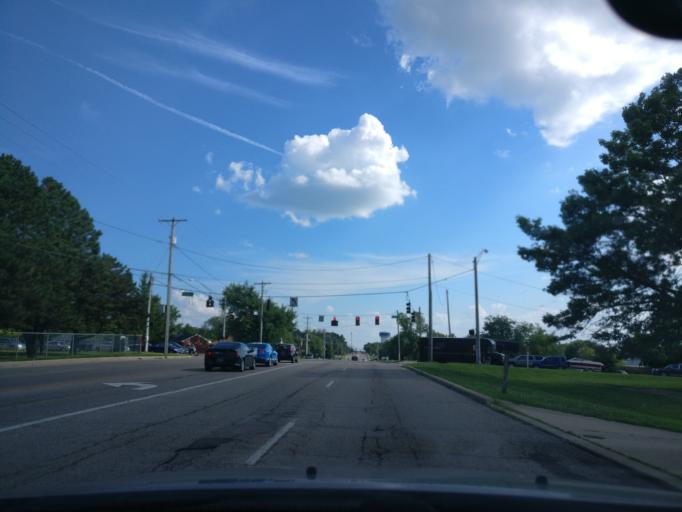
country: US
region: Ohio
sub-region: Montgomery County
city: West Carrollton City
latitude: 39.6324
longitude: -84.2351
